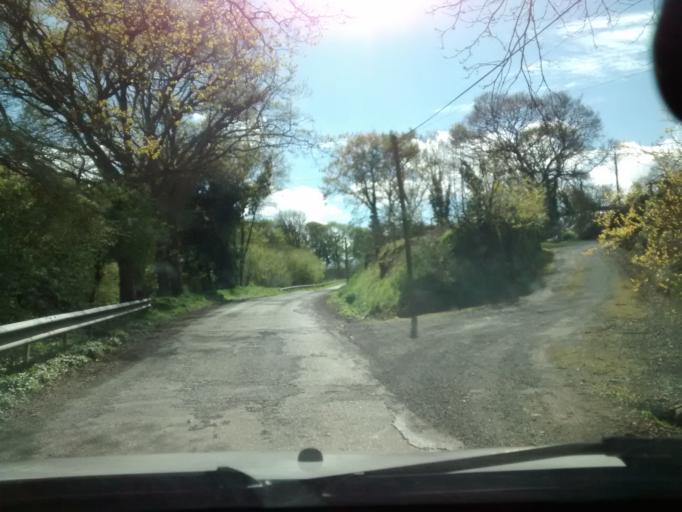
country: FR
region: Brittany
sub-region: Departement des Cotes-d'Armor
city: Langoat
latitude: 48.7753
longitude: -3.2882
